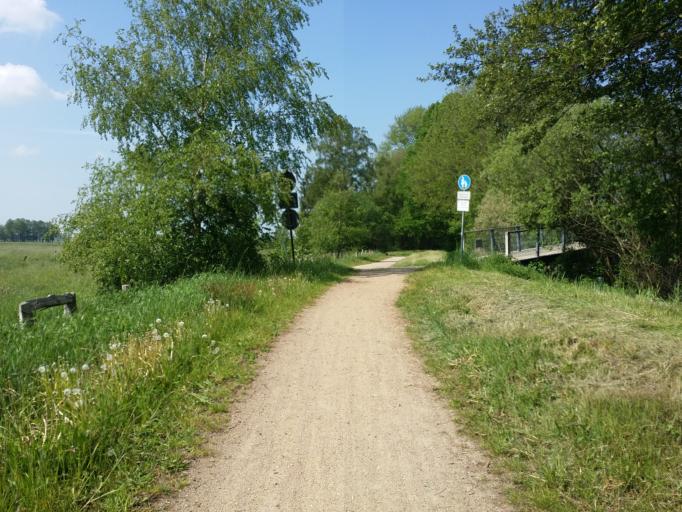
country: DE
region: Lower Saxony
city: Osterholz-Scharmbeck
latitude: 53.2147
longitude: 8.8599
